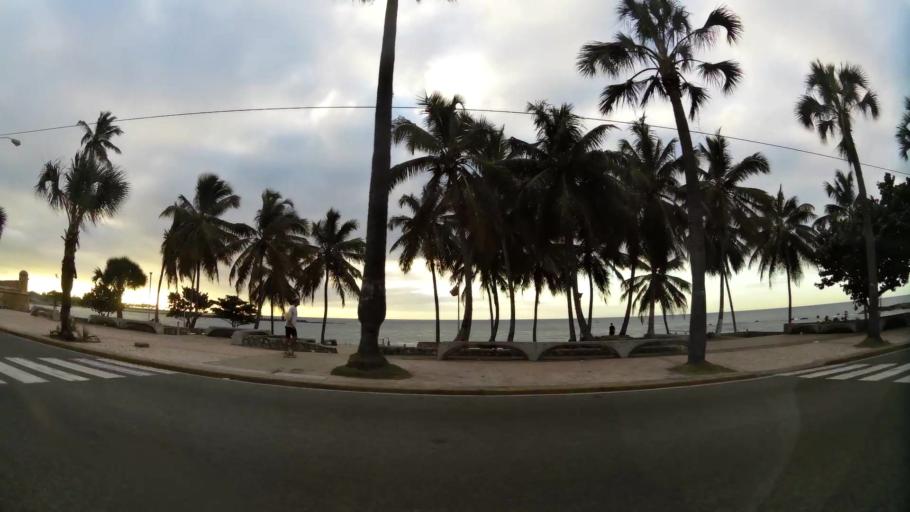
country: DO
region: Nacional
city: Ciudad Nueva
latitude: 18.4668
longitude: -69.8906
